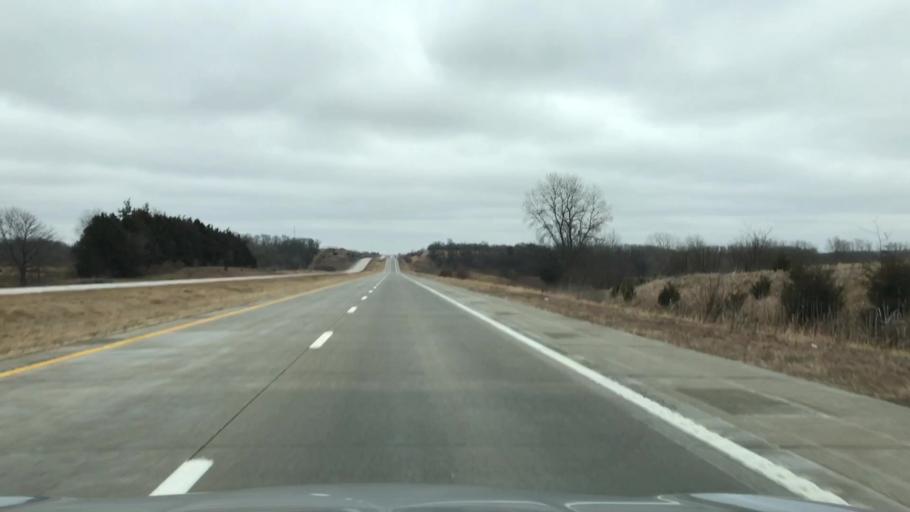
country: US
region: Missouri
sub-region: Caldwell County
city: Hamilton
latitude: 39.7350
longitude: -93.8291
